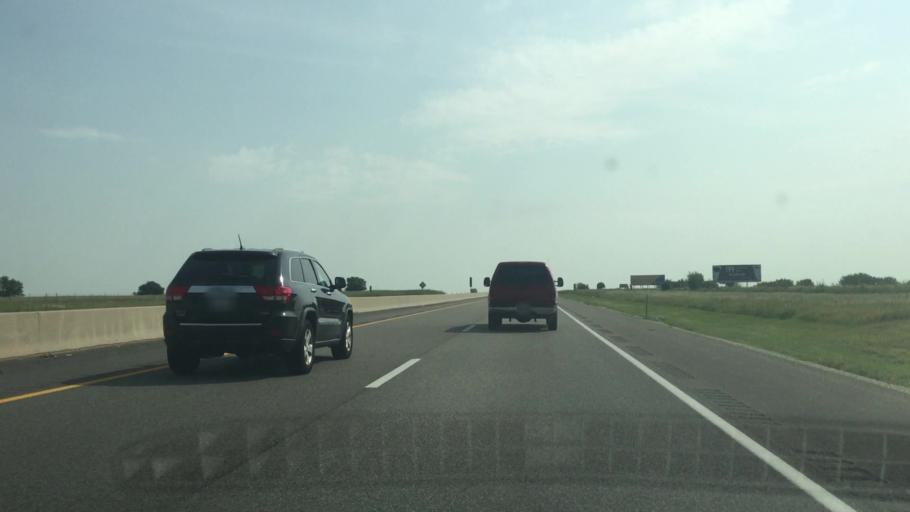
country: US
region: Kansas
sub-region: Butler County
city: Towanda
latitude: 37.7818
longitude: -96.9505
